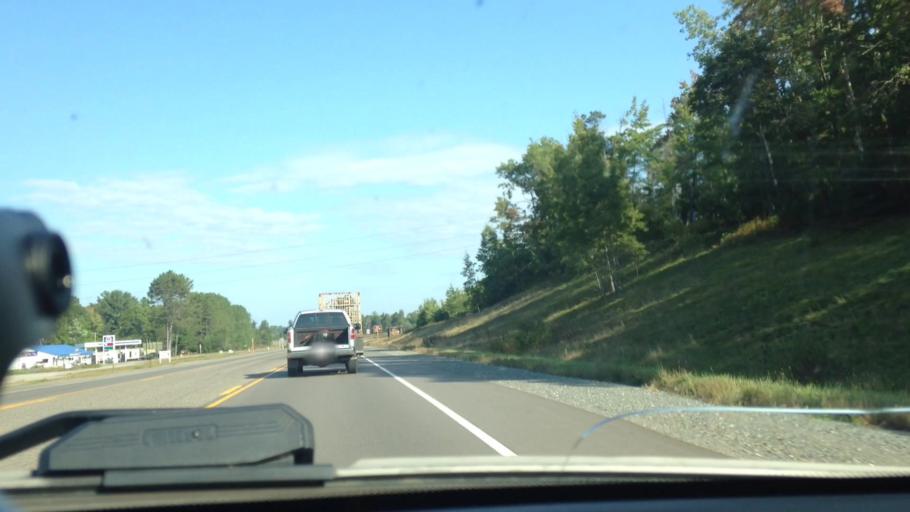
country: US
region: Michigan
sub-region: Dickinson County
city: Iron Mountain
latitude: 45.8690
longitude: -88.0821
